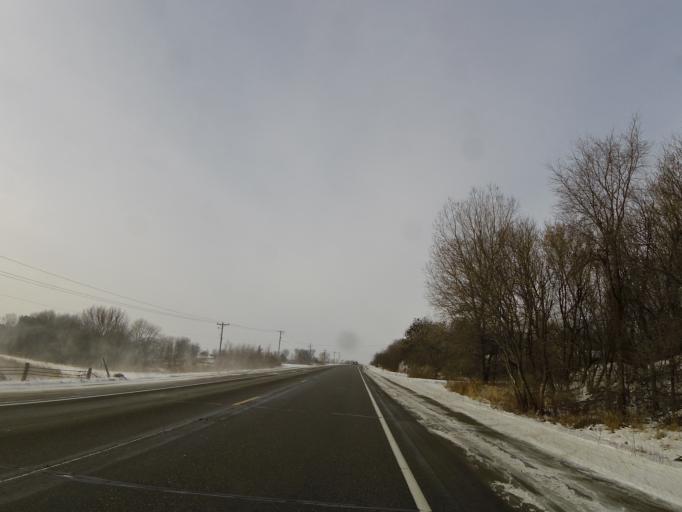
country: US
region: Minnesota
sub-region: Hennepin County
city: Saint Bonifacius
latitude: 44.9054
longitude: -93.7780
